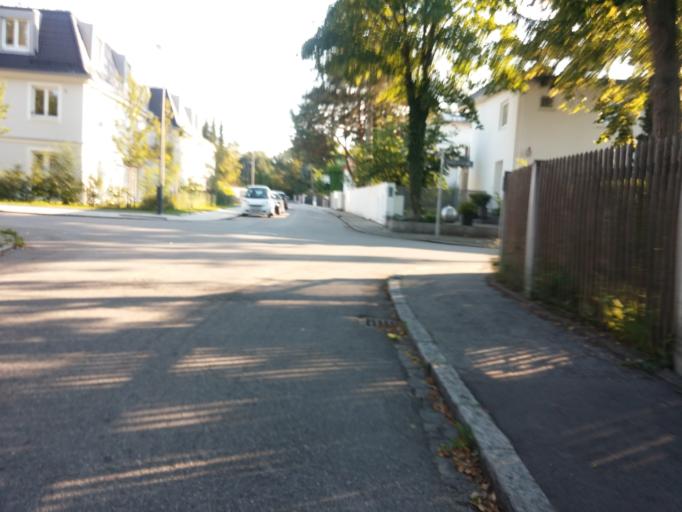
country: DE
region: Bavaria
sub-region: Upper Bavaria
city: Neubiberg
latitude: 48.1068
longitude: 11.6718
